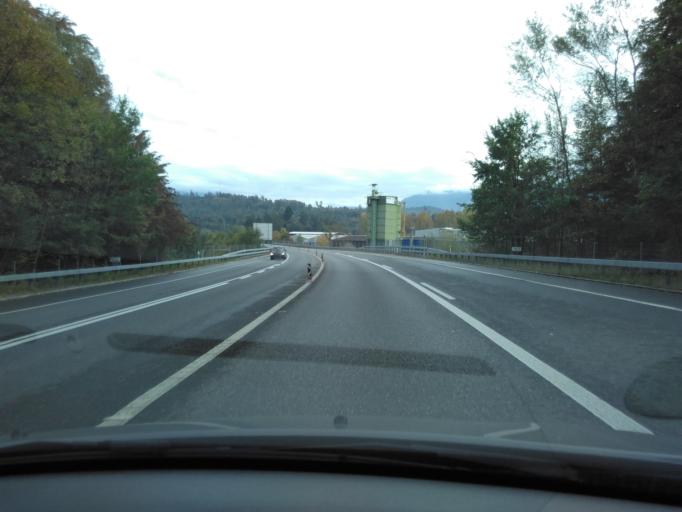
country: CH
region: Zurich
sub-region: Bezirk Hinwil
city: Rueti / Dorfzentrum, Suedl. Teil
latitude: 47.2293
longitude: 8.8682
